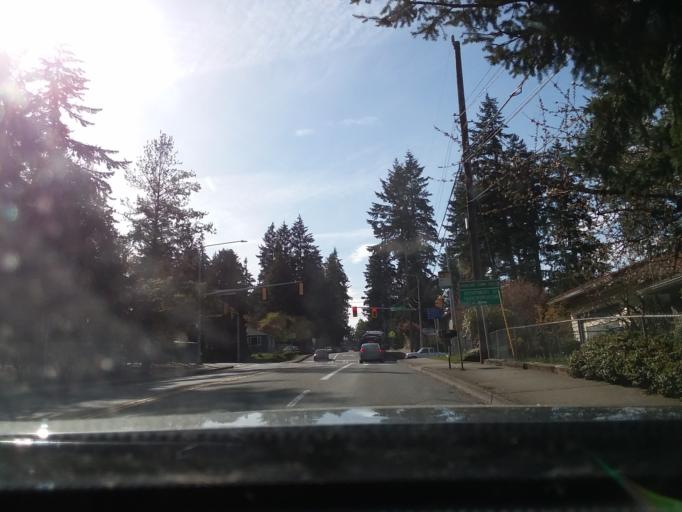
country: US
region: Washington
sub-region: King County
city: Shoreline
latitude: 47.7451
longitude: -122.3525
